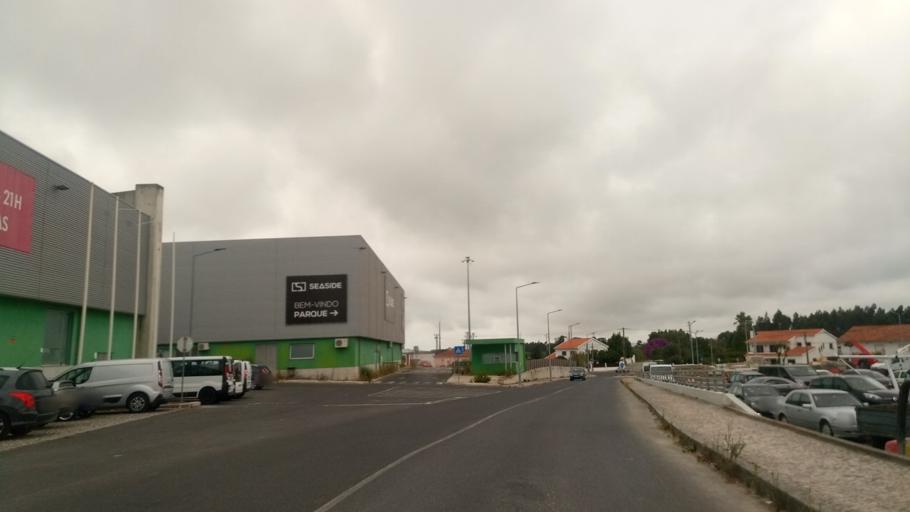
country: PT
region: Leiria
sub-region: Caldas da Rainha
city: Caldas da Rainha
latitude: 39.4134
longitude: -9.1412
